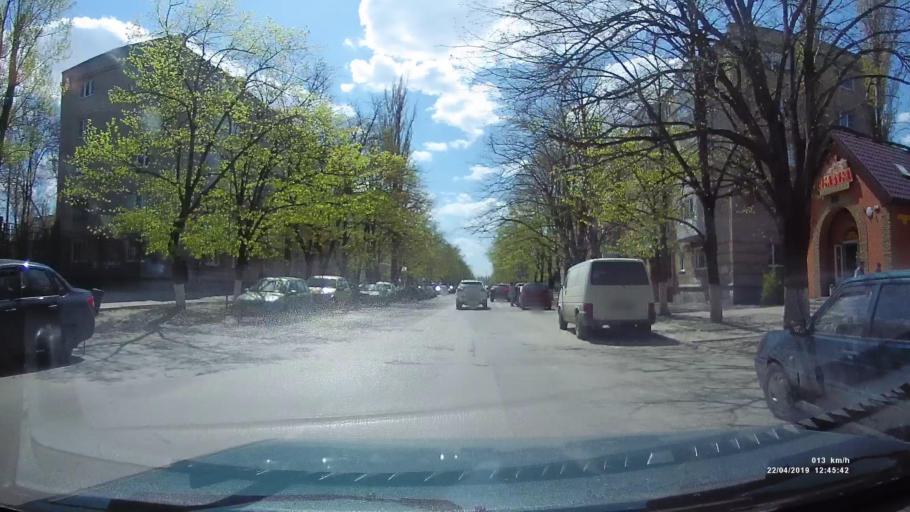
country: RU
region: Rostov
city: Azov
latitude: 47.1028
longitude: 39.4137
